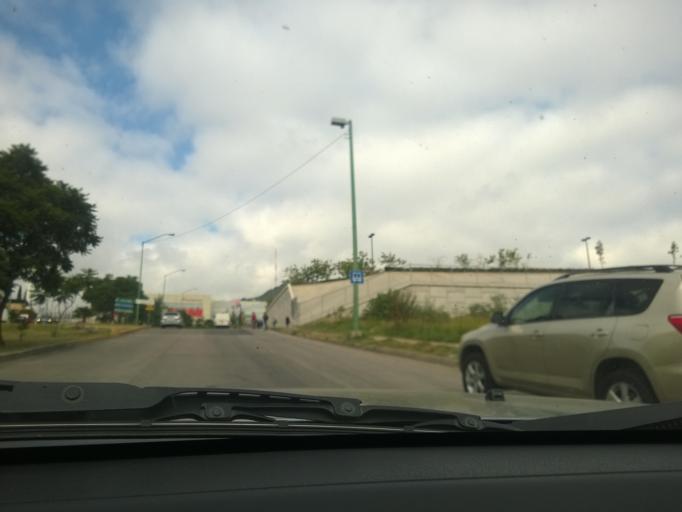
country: MX
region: Guanajuato
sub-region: Leon
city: La Ermita
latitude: 21.1556
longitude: -101.7047
